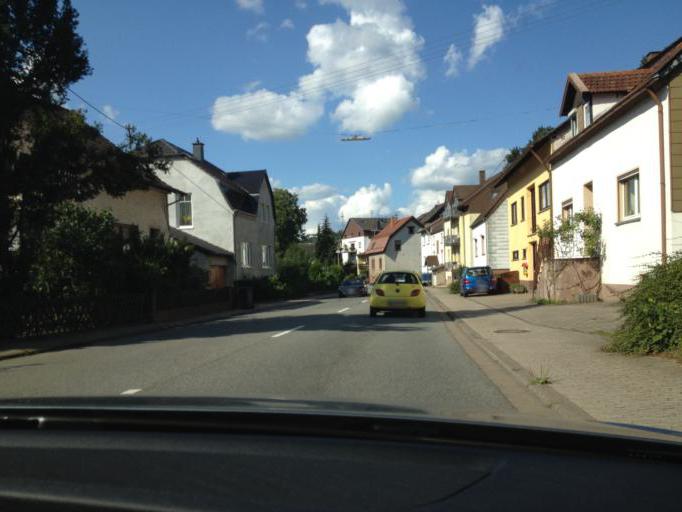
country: DE
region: Saarland
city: Illingen
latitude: 49.4111
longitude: 7.0157
